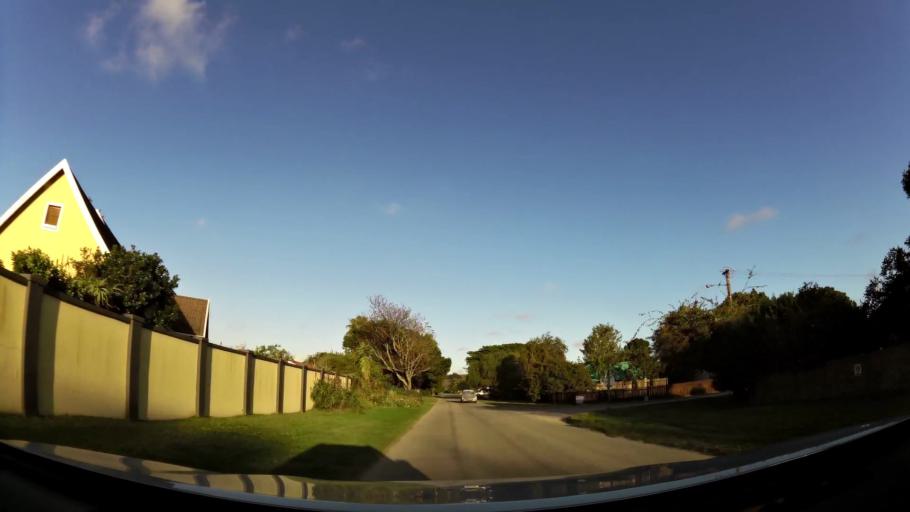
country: ZA
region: Western Cape
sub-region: Eden District Municipality
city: Knysna
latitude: -34.0142
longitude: 22.7823
